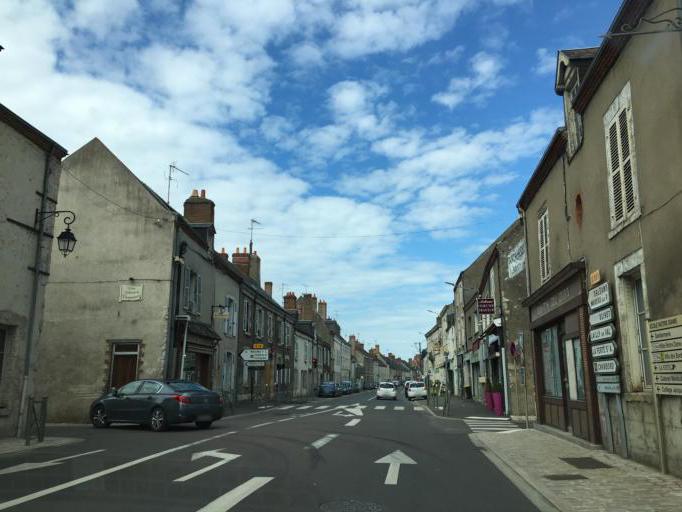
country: FR
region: Centre
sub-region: Departement du Loiret
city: Clery-Saint-Andre
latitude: 47.8206
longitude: 1.7553
